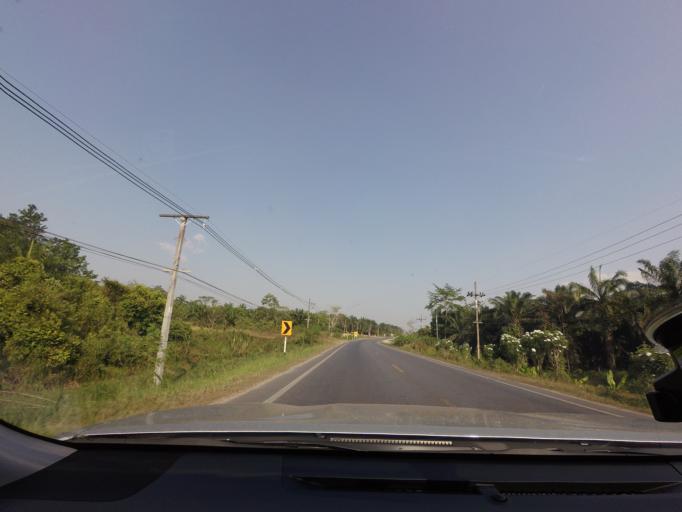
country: TH
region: Surat Thani
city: Phrasaeng
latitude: 8.5601
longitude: 99.1604
